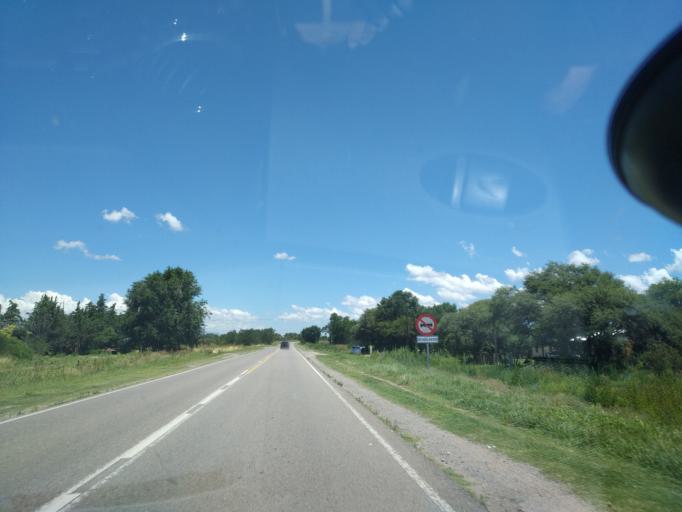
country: AR
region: Cordoba
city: Salsacate
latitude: -31.4893
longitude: -65.1079
